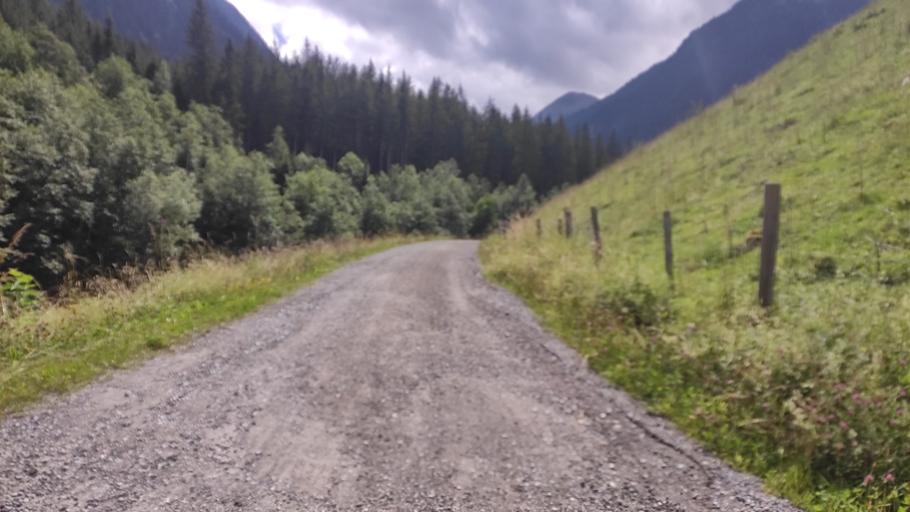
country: AT
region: Salzburg
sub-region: Politischer Bezirk Zell am See
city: Krimml
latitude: 47.2154
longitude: 12.1737
